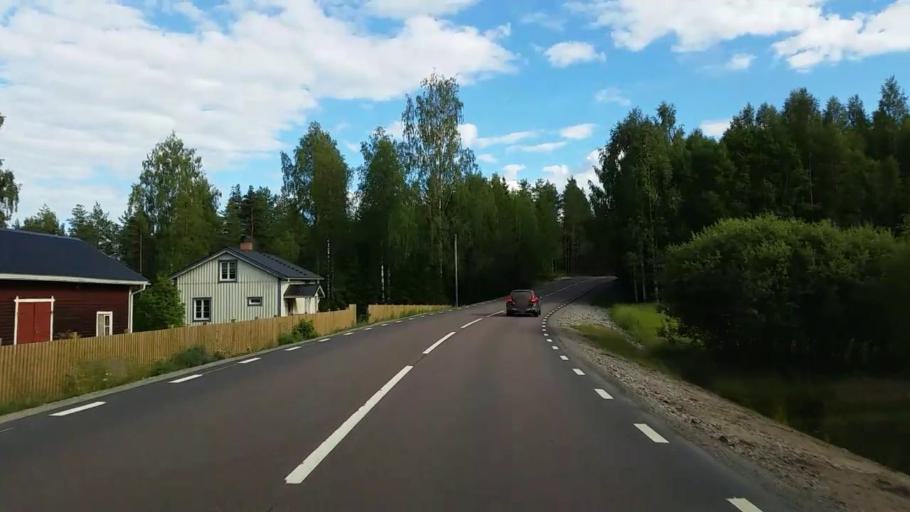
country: SE
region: Gaevleborg
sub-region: Ljusdals Kommun
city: Ljusdal
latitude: 61.8661
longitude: 15.9824
